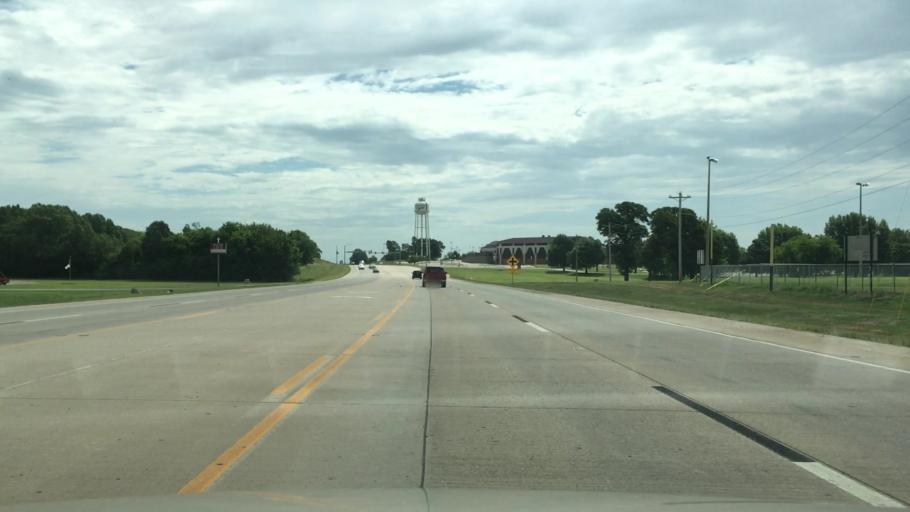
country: US
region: Oklahoma
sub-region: Cherokee County
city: Park Hill
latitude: 35.8492
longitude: -95.0080
